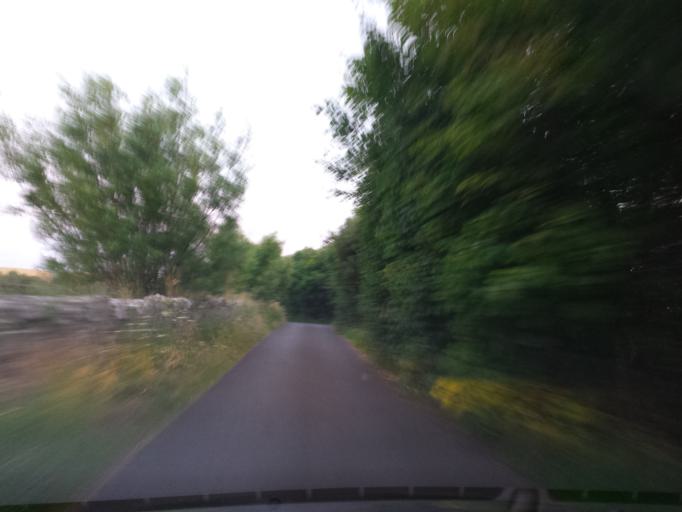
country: GB
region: Scotland
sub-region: The Scottish Borders
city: Eyemouth
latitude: 55.8646
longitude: -2.0848
